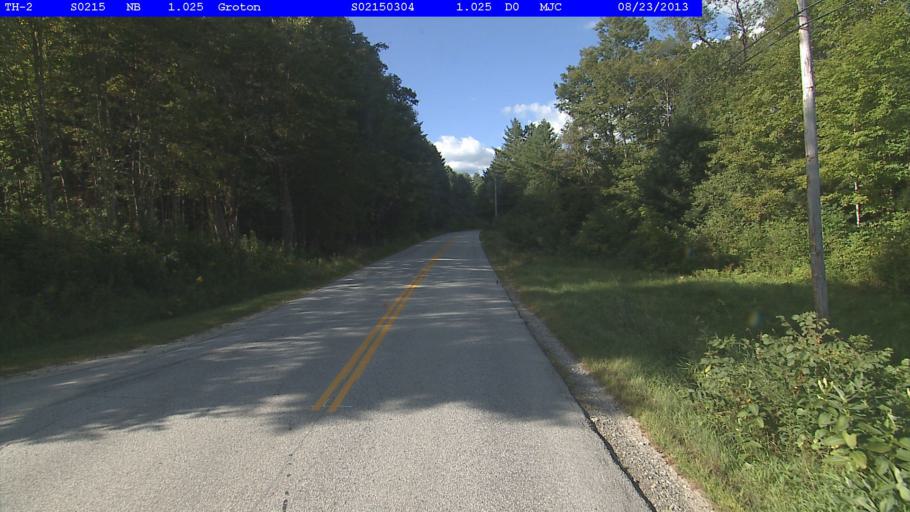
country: US
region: New Hampshire
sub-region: Grafton County
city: Woodsville
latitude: 44.2235
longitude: -72.1908
